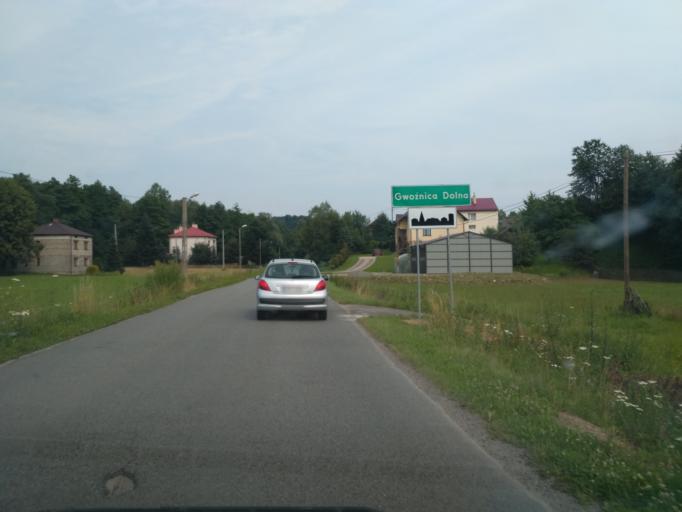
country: PL
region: Subcarpathian Voivodeship
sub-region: Powiat strzyzowski
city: Konieczkowa
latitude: 49.8387
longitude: 21.9485
